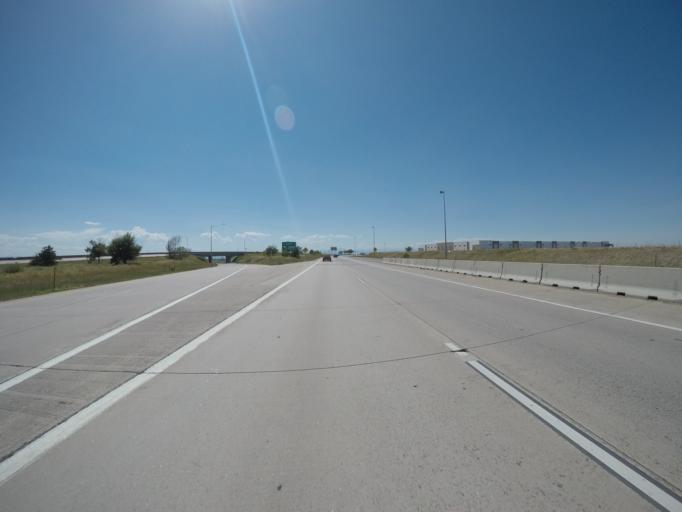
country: US
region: Colorado
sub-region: Adams County
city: Aurora
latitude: 39.7409
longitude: -104.7308
